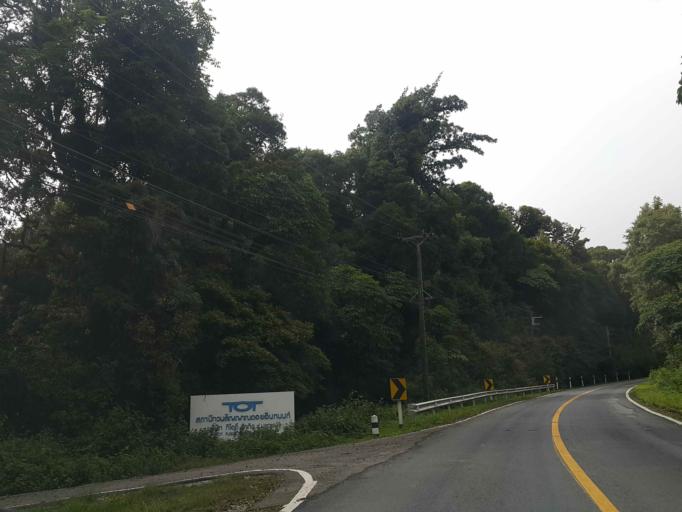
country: TH
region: Chiang Mai
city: Mae Chaem
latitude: 18.5754
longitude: 98.4823
